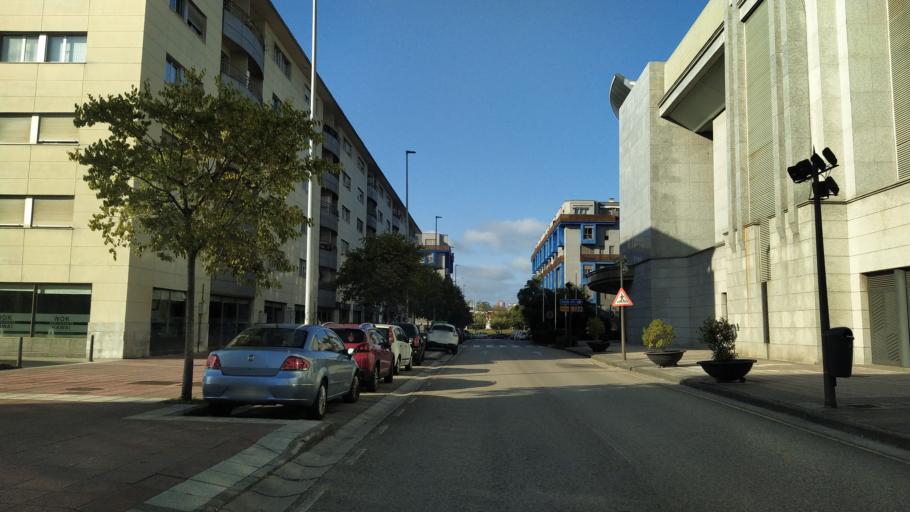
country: ES
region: Cantabria
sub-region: Provincia de Cantabria
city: El Astillero
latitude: 43.4378
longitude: -3.8411
